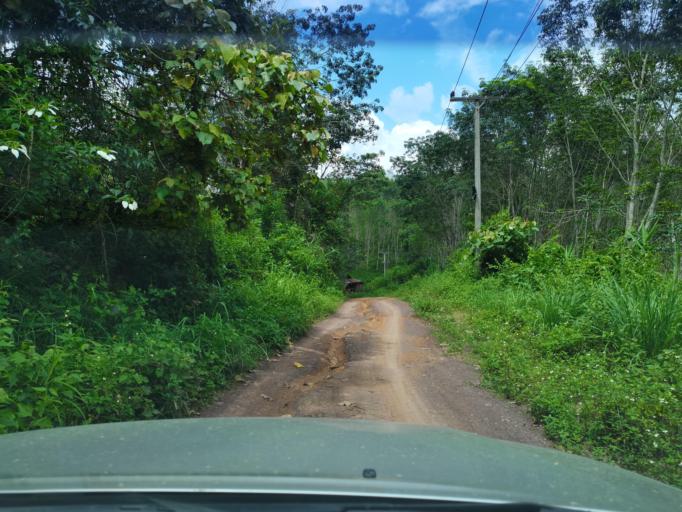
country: LA
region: Loungnamtha
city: Muang Long
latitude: 20.7008
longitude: 101.0276
